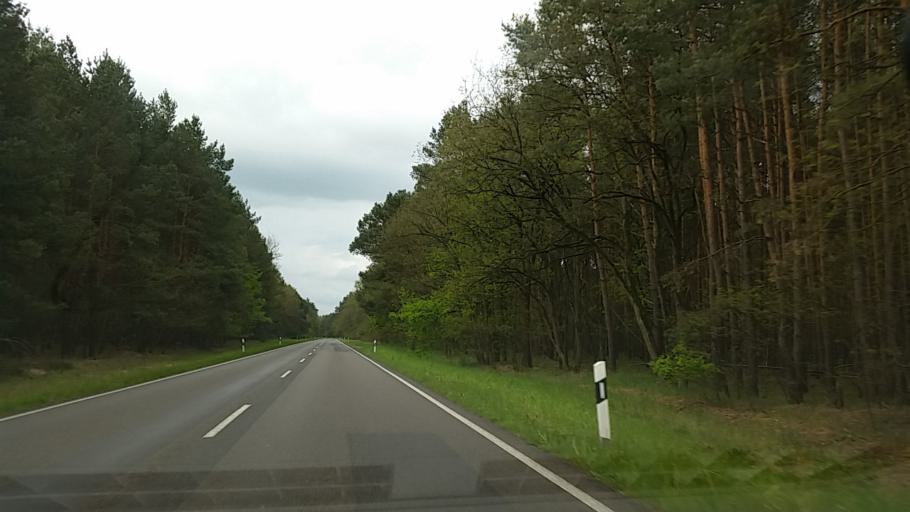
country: DE
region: Brandenburg
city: Storkow
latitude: 52.3024
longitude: 13.9025
